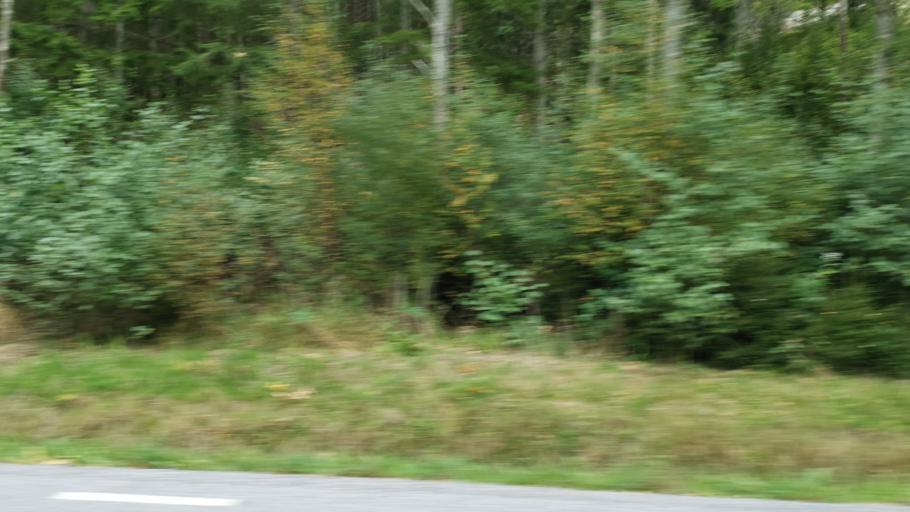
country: SE
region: Vaestra Goetaland
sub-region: Tanums Kommun
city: Tanumshede
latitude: 58.7035
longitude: 11.3377
